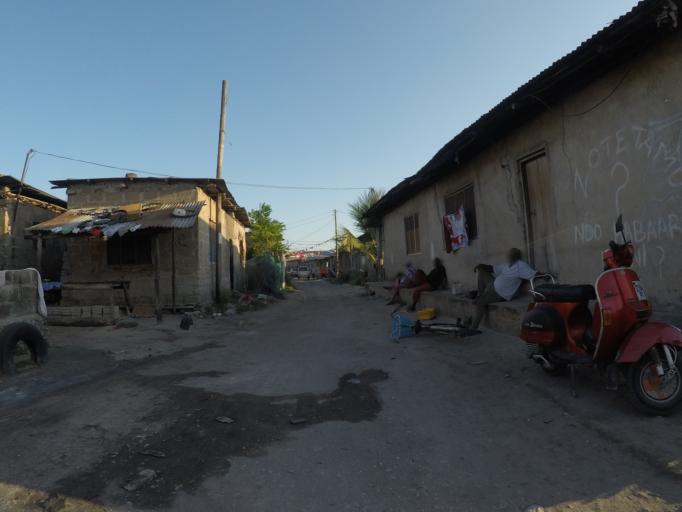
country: TZ
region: Zanzibar Urban/West
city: Zanzibar
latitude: -6.1589
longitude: 39.2178
